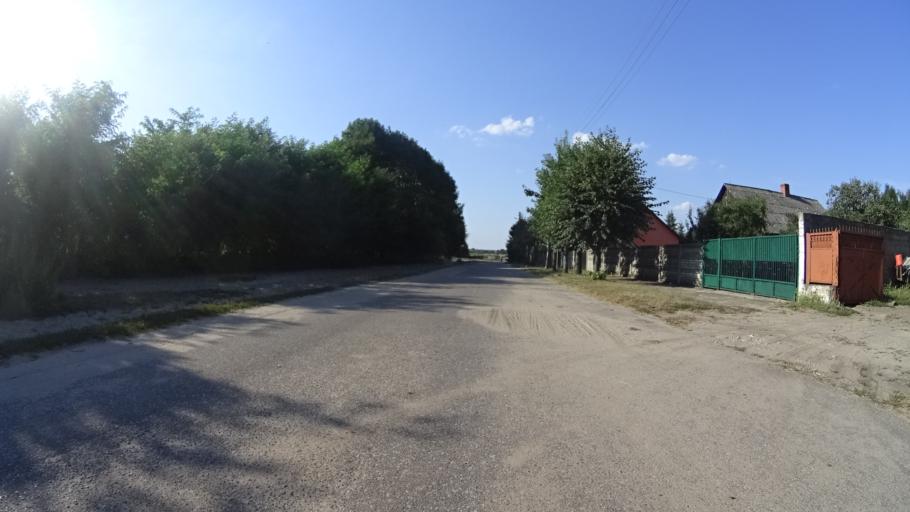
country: PL
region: Masovian Voivodeship
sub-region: Powiat bialobrzeski
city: Wysmierzyce
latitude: 51.6275
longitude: 20.8175
